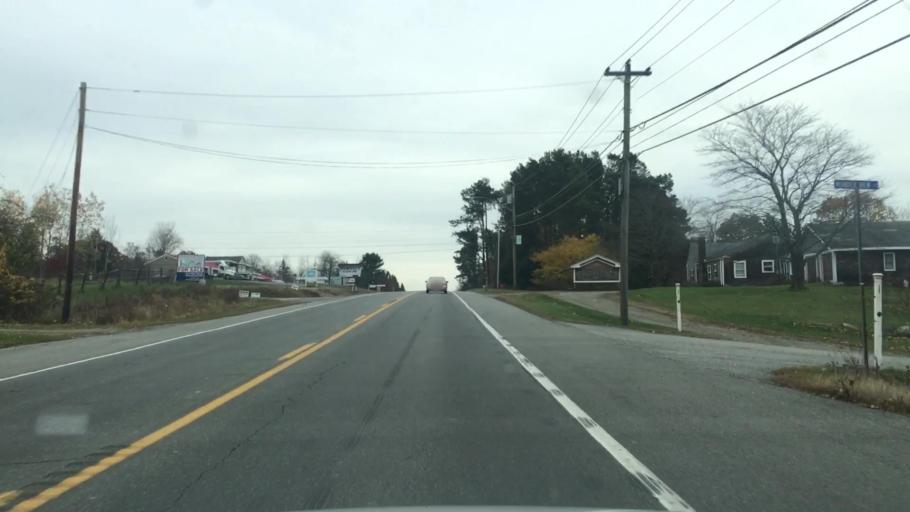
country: US
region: Maine
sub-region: Waldo County
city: Belfast
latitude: 44.4303
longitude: -68.9681
